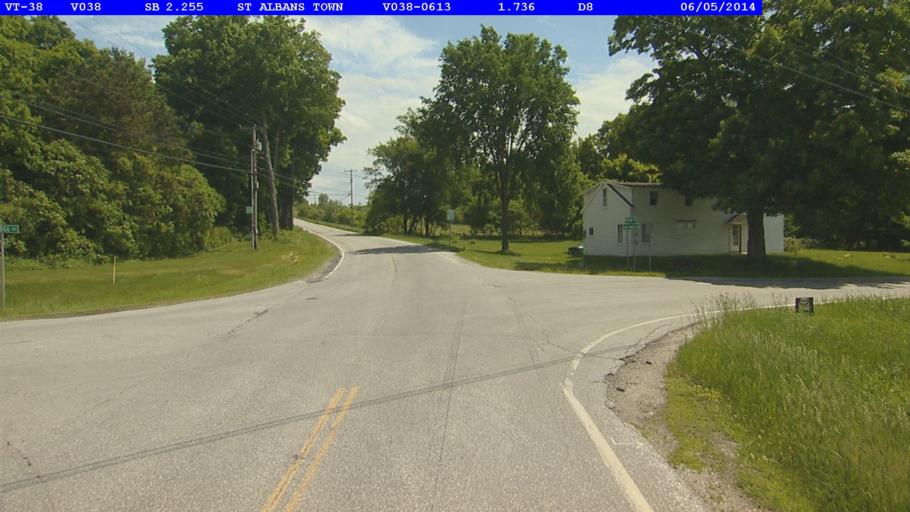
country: US
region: Vermont
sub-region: Franklin County
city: Saint Albans
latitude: 44.8443
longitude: -73.1090
